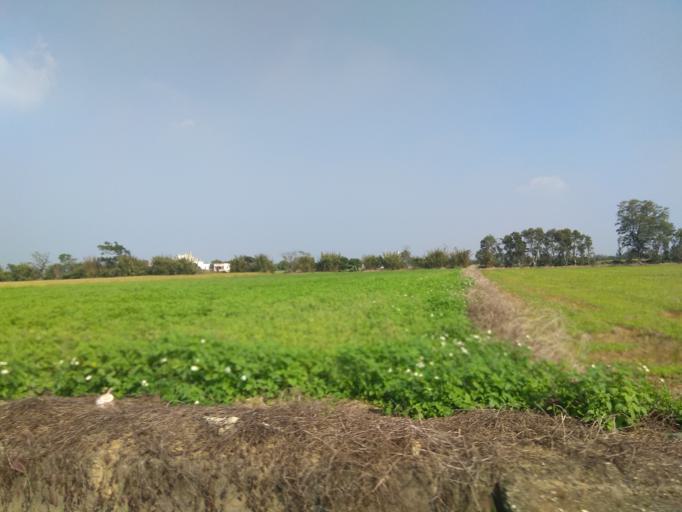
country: TW
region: Taiwan
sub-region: Hsinchu
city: Zhubei
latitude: 24.9974
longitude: 121.0610
